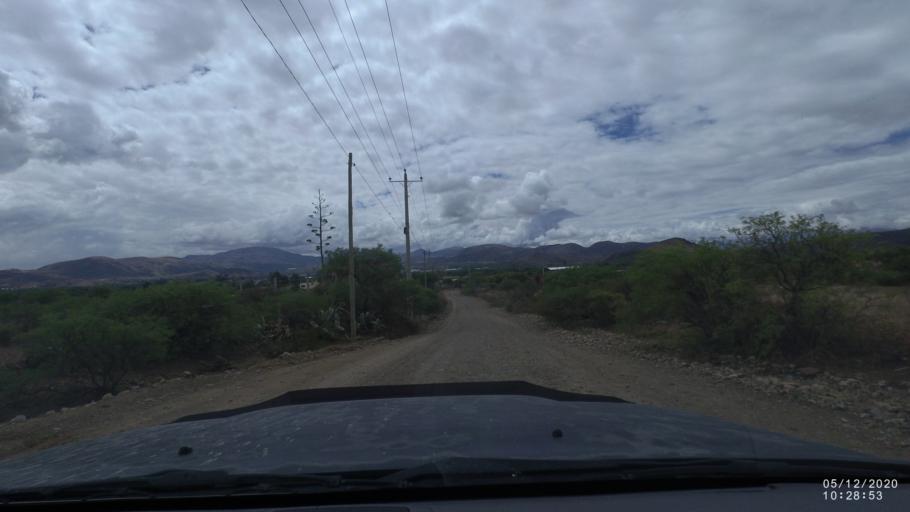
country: BO
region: Cochabamba
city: Sipe Sipe
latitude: -17.5401
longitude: -66.2704
